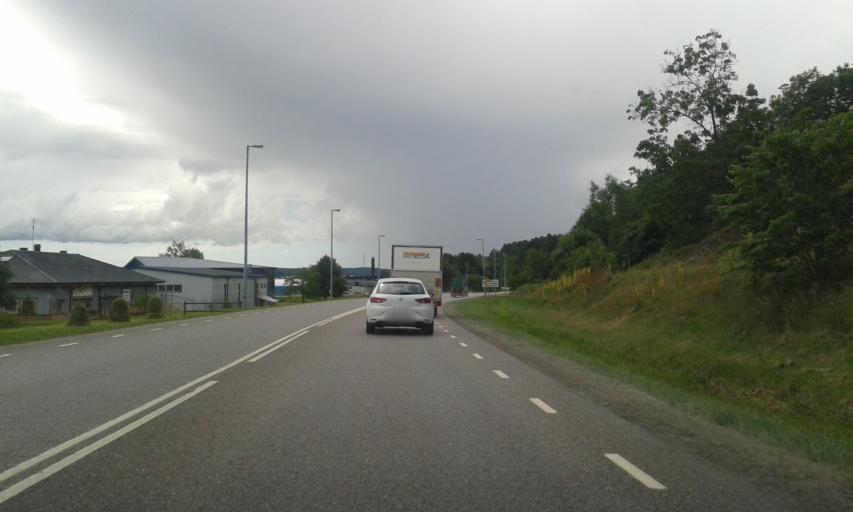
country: SE
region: Vaestra Goetaland
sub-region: Kungalvs Kommun
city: Kungalv
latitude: 57.8887
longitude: 11.9882
